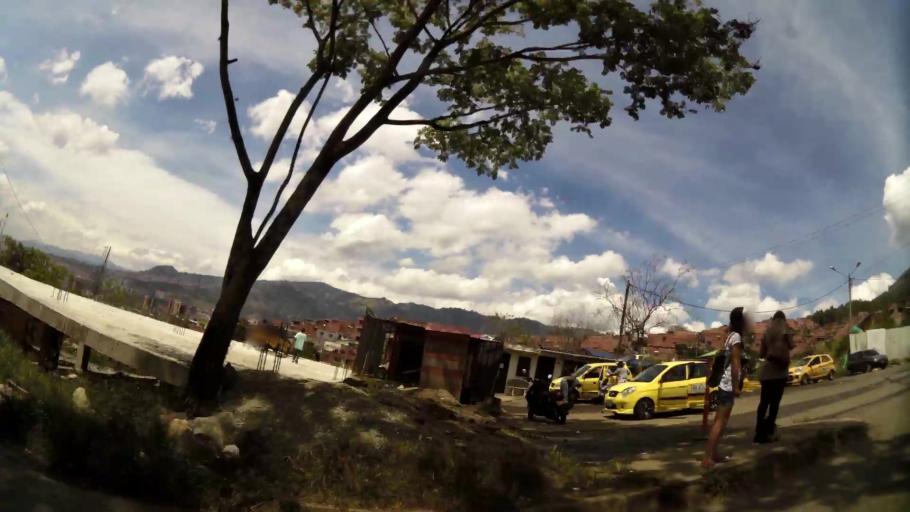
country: CO
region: Antioquia
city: Bello
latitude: 6.3480
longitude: -75.5464
